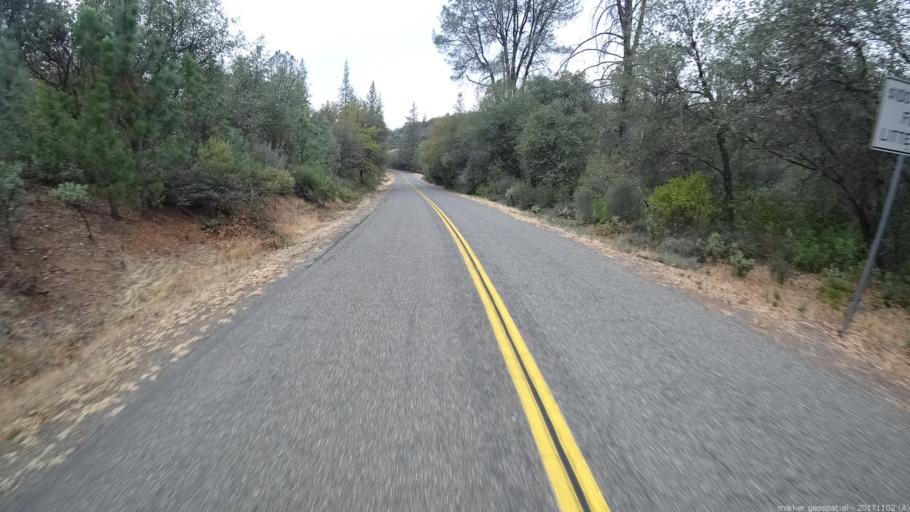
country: US
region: California
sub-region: Shasta County
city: Central Valley (historical)
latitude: 40.6599
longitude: -122.4186
